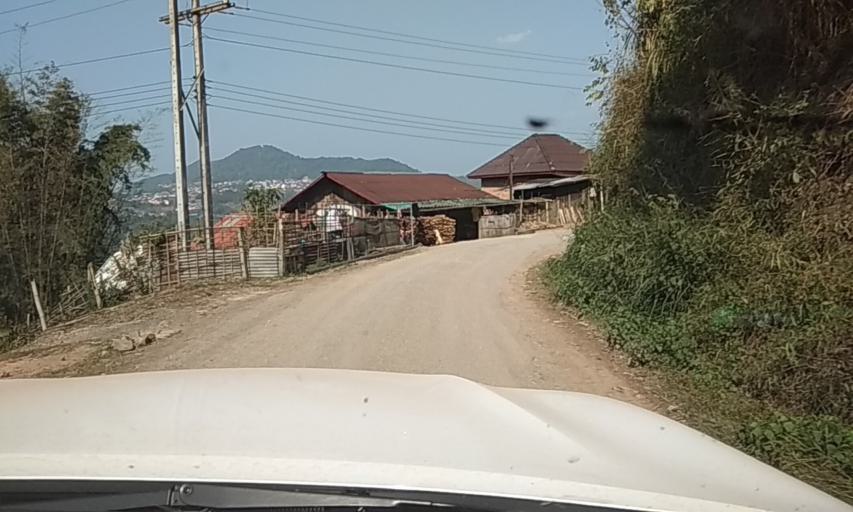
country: LA
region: Phongsali
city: Phongsali
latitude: 21.6610
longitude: 102.0904
